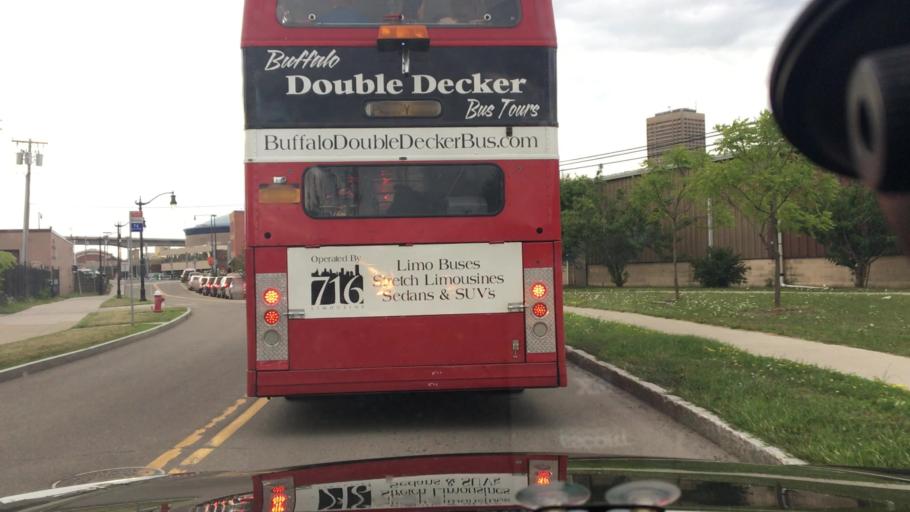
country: US
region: New York
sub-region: Erie County
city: Buffalo
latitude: 42.8714
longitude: -78.8706
